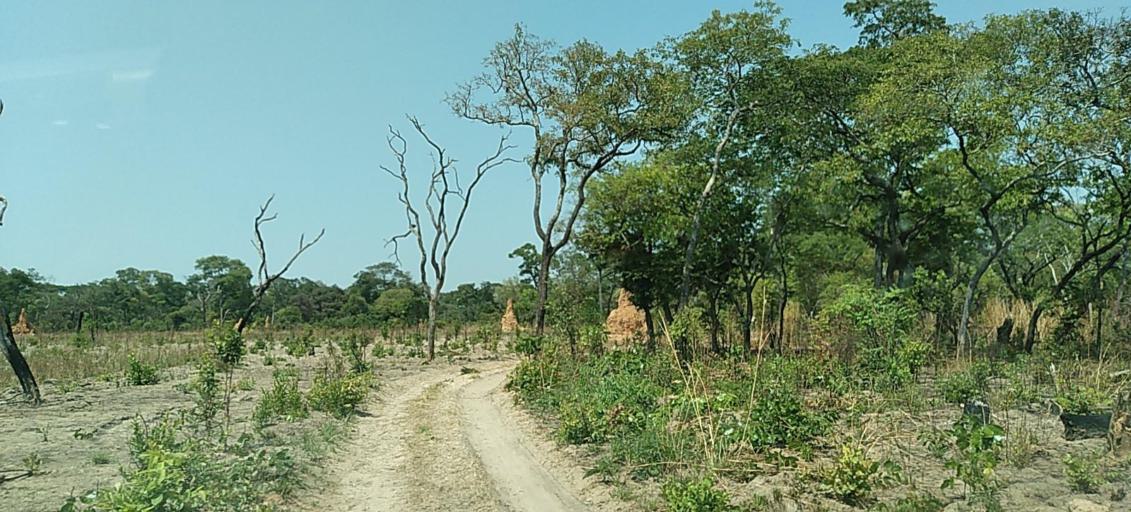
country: ZM
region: Copperbelt
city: Mpongwe
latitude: -13.7903
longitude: 28.0938
